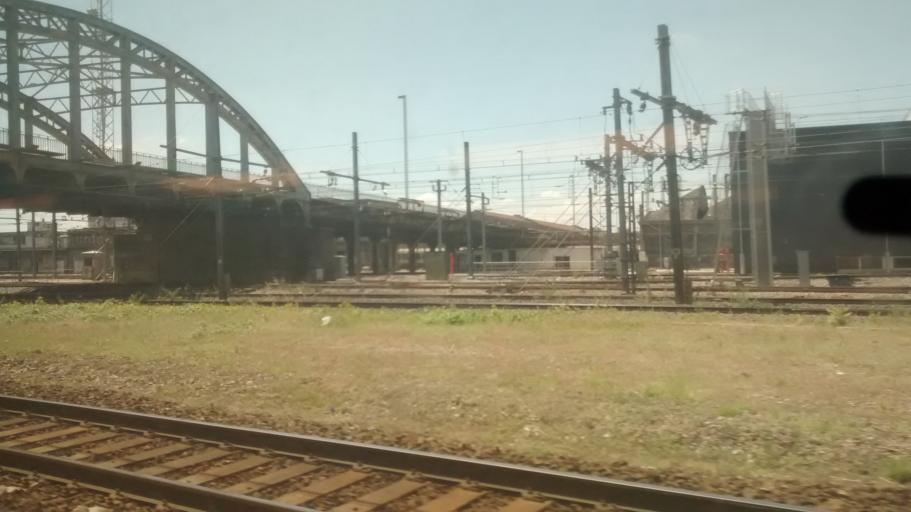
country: FR
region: Rhone-Alpes
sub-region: Departement du Rhone
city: Lyon
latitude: 45.7374
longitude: 4.8490
